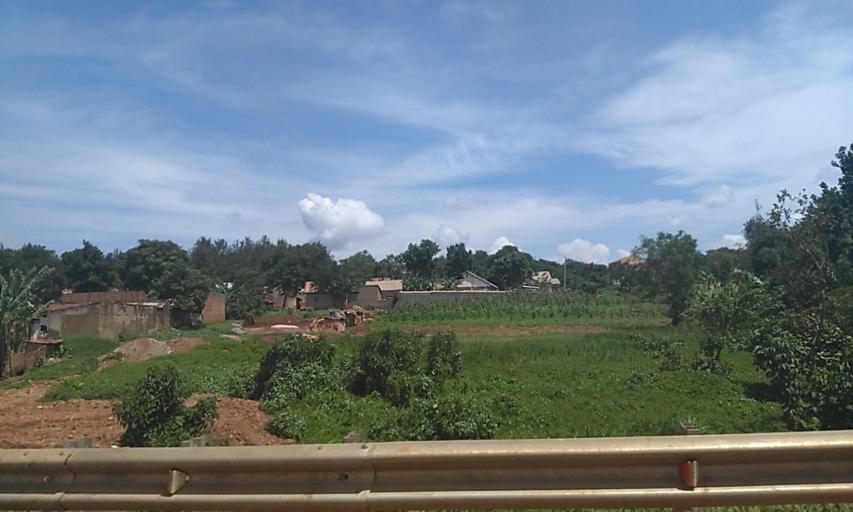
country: UG
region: Central Region
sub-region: Wakiso District
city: Wakiso
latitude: 0.4014
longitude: 32.4772
